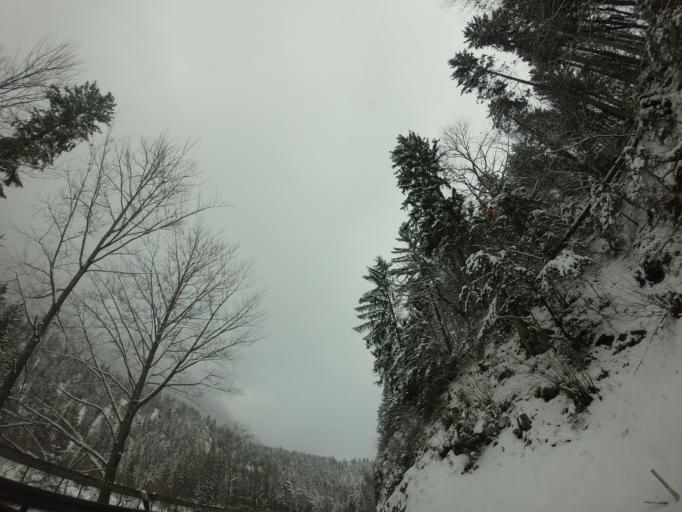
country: DE
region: Bavaria
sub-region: Upper Bavaria
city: Grainau
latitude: 47.4827
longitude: 11.0285
